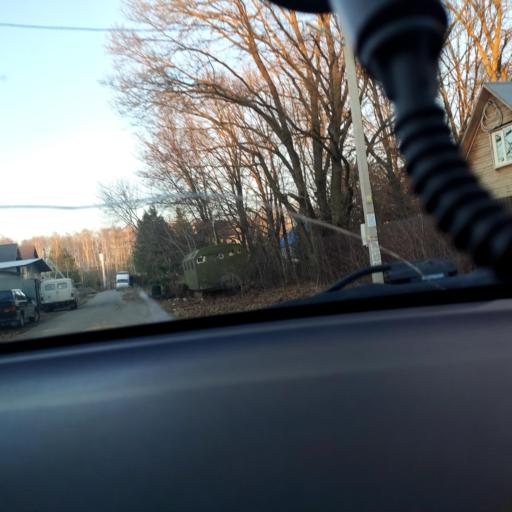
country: RU
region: Tatarstan
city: Osinovo
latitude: 55.8535
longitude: 48.9157
